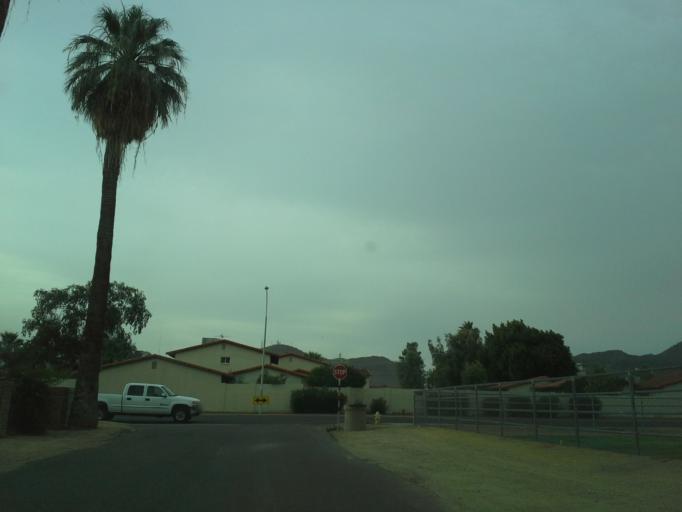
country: US
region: Arizona
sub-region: Maricopa County
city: Glendale
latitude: 33.5672
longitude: -112.0869
